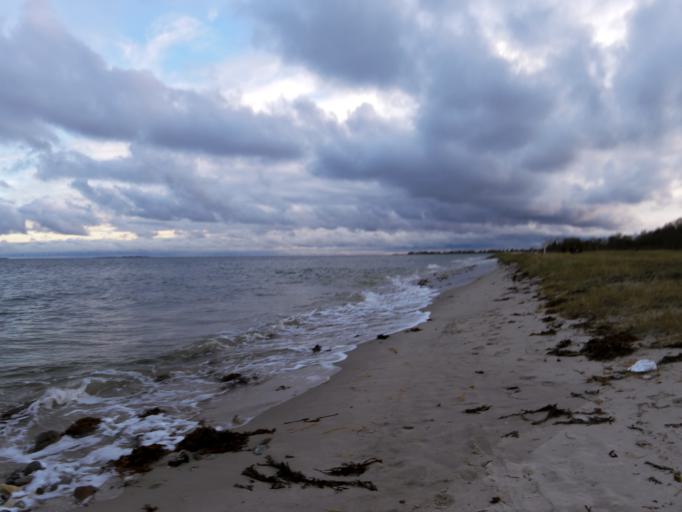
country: DK
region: Central Jutland
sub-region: Arhus Kommune
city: Beder
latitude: 56.0475
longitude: 10.2712
